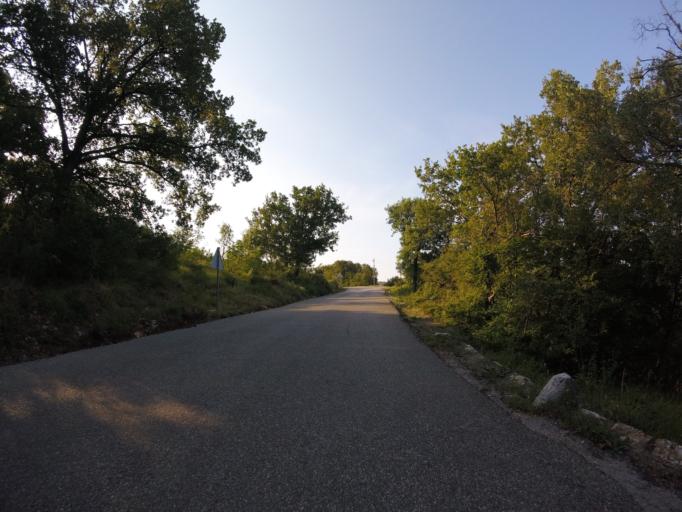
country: HR
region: Primorsko-Goranska
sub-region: Grad Crikvenica
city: Crikvenica
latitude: 45.1908
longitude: 14.7206
